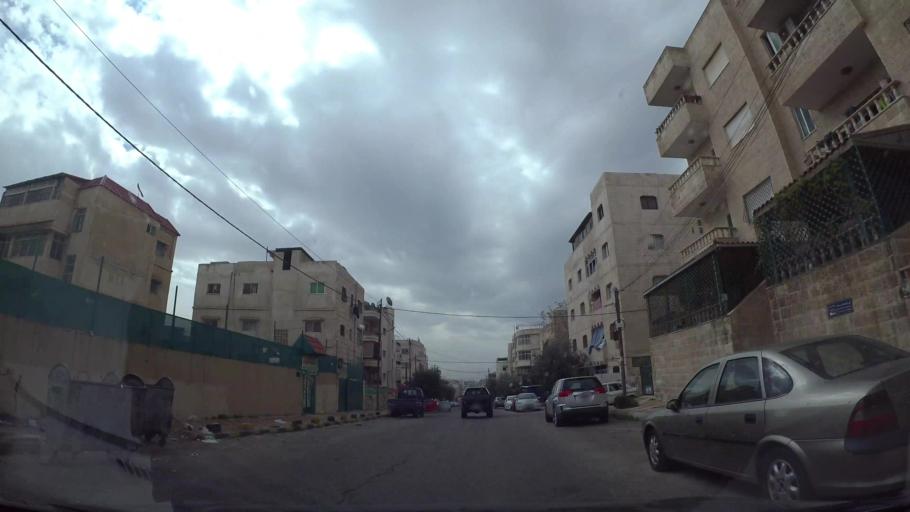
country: JO
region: Amman
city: Amman
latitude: 31.9827
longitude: 35.9275
